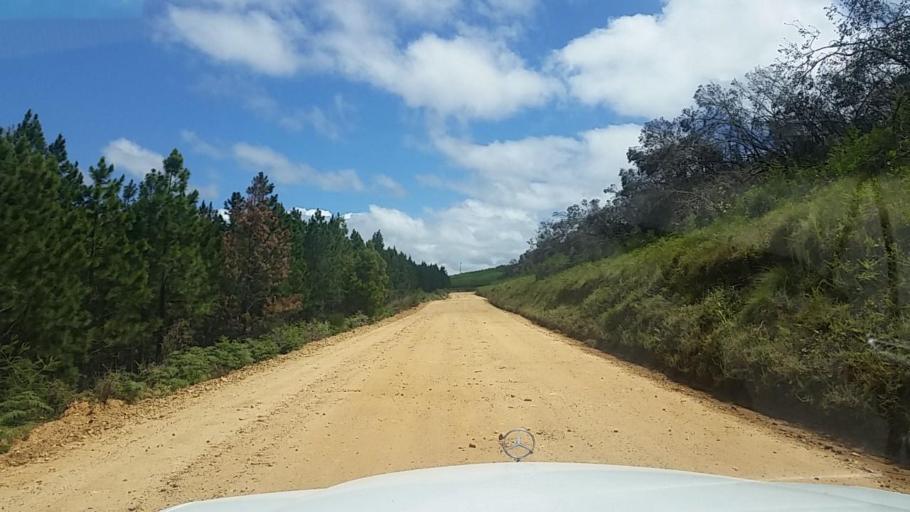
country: ZA
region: Western Cape
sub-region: Eden District Municipality
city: Knysna
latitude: -33.8917
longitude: 23.1663
